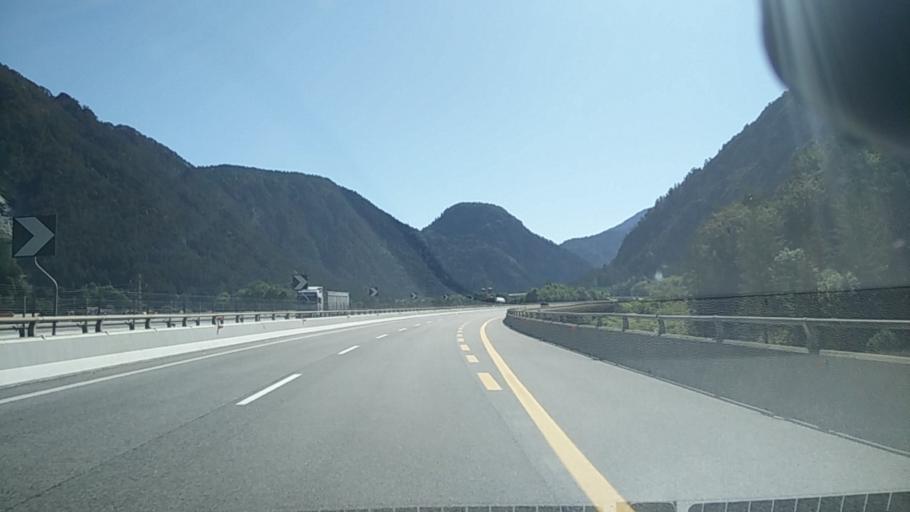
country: IT
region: Friuli Venezia Giulia
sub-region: Provincia di Udine
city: Malborghetto
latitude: 46.5086
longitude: 13.4658
